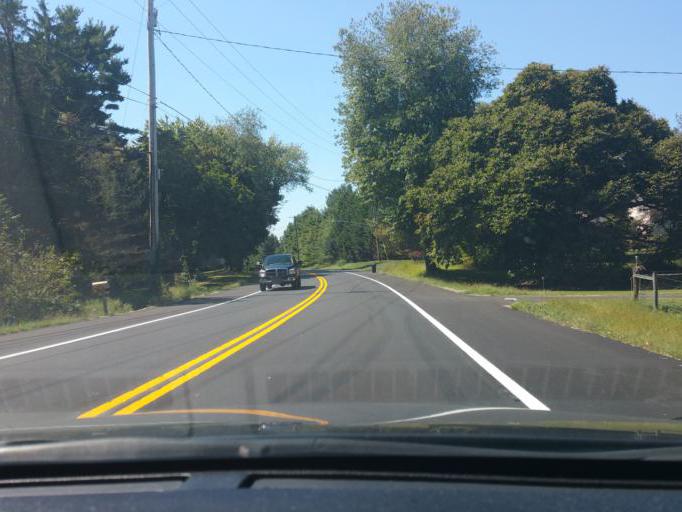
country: US
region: Maryland
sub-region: Harford County
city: Aberdeen
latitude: 39.5737
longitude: -76.2157
